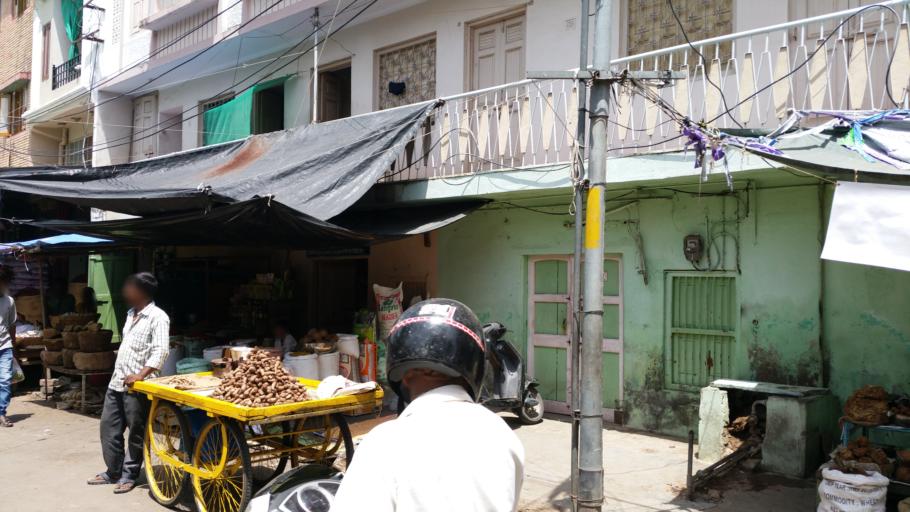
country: IN
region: Rajasthan
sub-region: Udaipur
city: Udaipur
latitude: 24.5829
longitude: 73.6941
